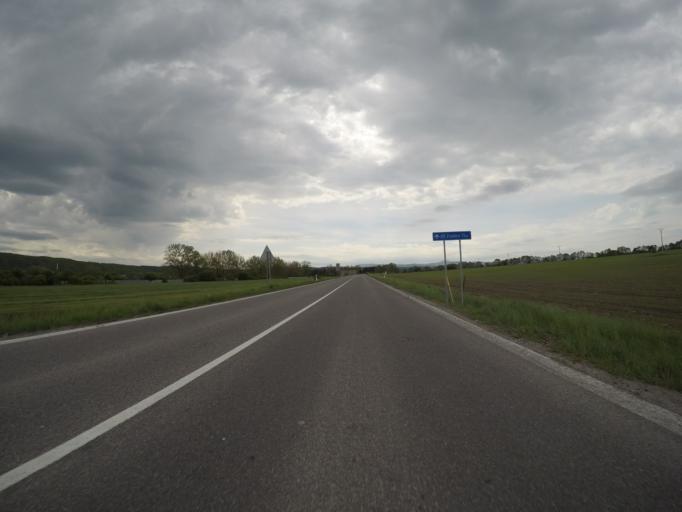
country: SK
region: Banskobystricky
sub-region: Okres Banska Bystrica
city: Banska Bystrica
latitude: 48.6655
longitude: 19.1402
